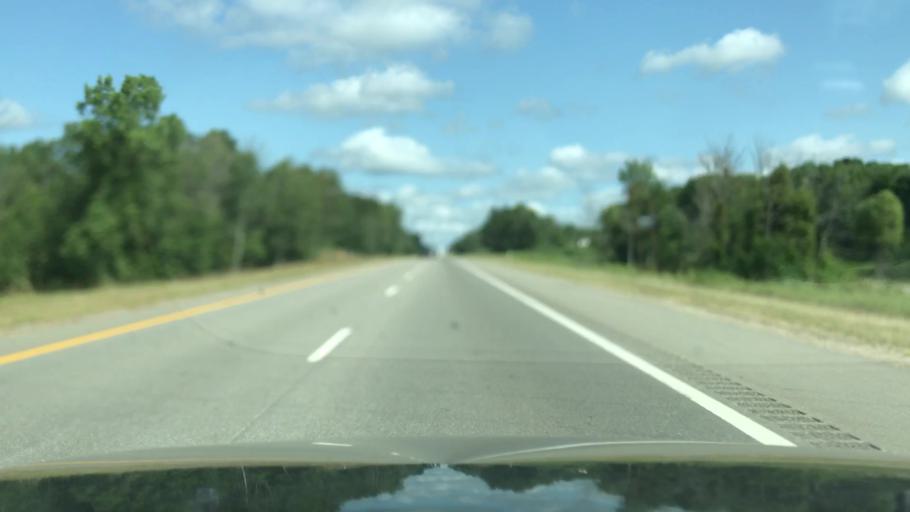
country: US
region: Michigan
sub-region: Mecosta County
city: Big Rapids
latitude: 43.6279
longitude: -85.5019
